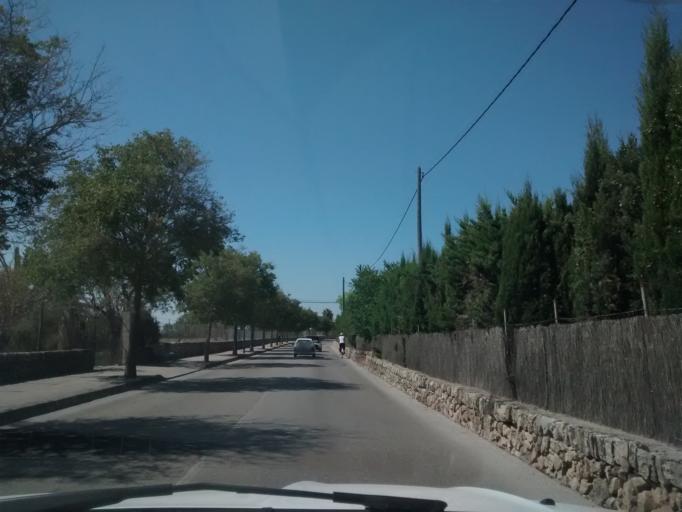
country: ES
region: Balearic Islands
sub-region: Illes Balears
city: Alcudia
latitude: 39.8549
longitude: 3.1315
